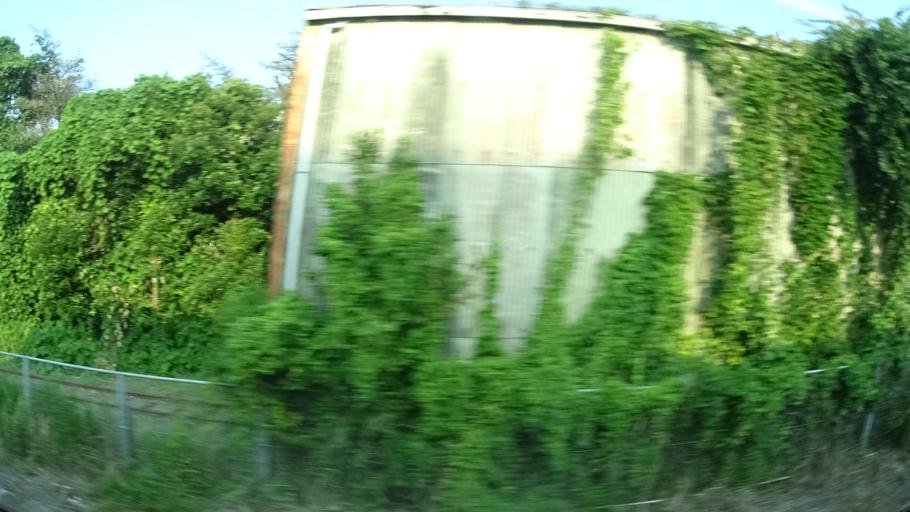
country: JP
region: Ibaraki
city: Hitachi
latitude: 36.5579
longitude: 140.6385
